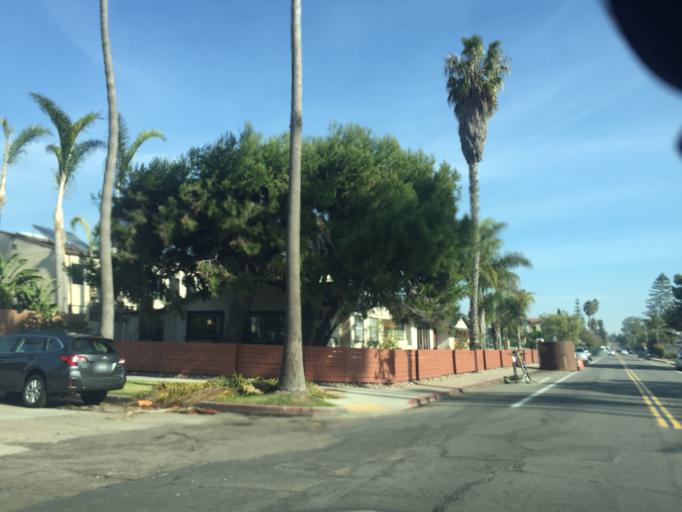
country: US
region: California
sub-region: San Diego County
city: La Jolla
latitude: 32.7914
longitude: -117.2520
